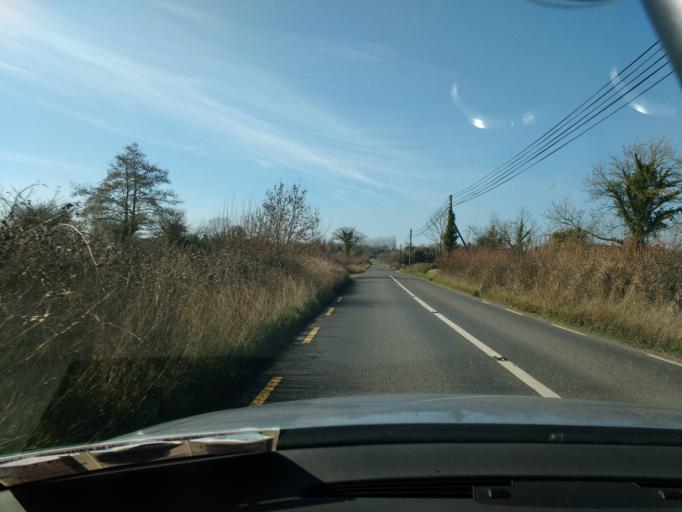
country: IE
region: Munster
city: Thurles
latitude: 52.6889
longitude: -7.8729
